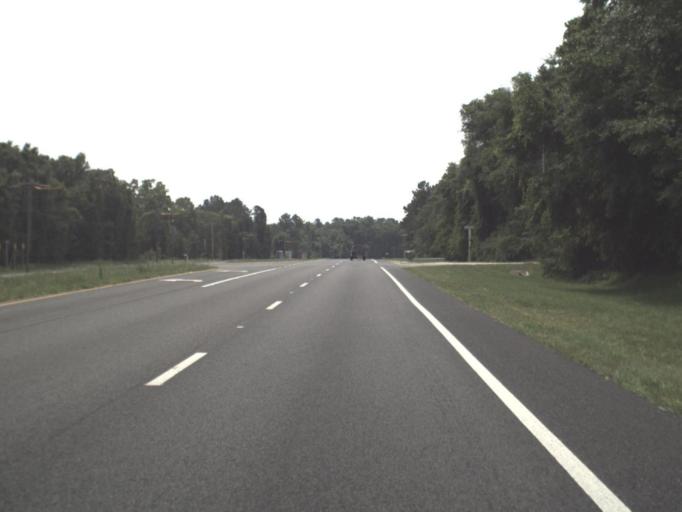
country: US
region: Florida
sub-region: Clay County
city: Green Cove Springs
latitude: 29.8840
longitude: -81.6662
